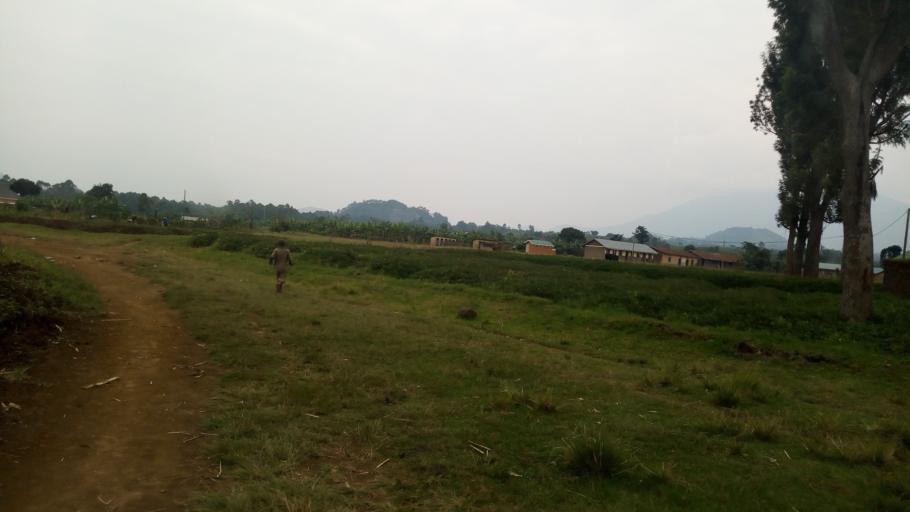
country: UG
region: Western Region
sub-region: Kisoro District
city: Kisoro
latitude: -1.2736
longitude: 29.6222
